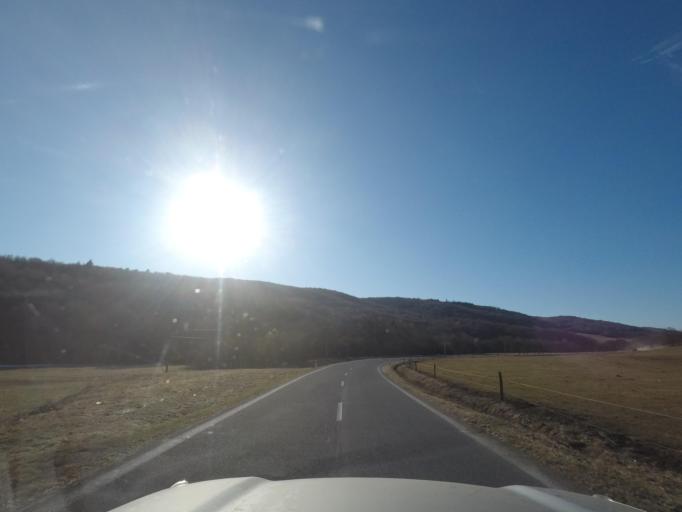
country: SK
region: Presovsky
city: Medzilaborce
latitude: 49.1794
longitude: 22.0200
